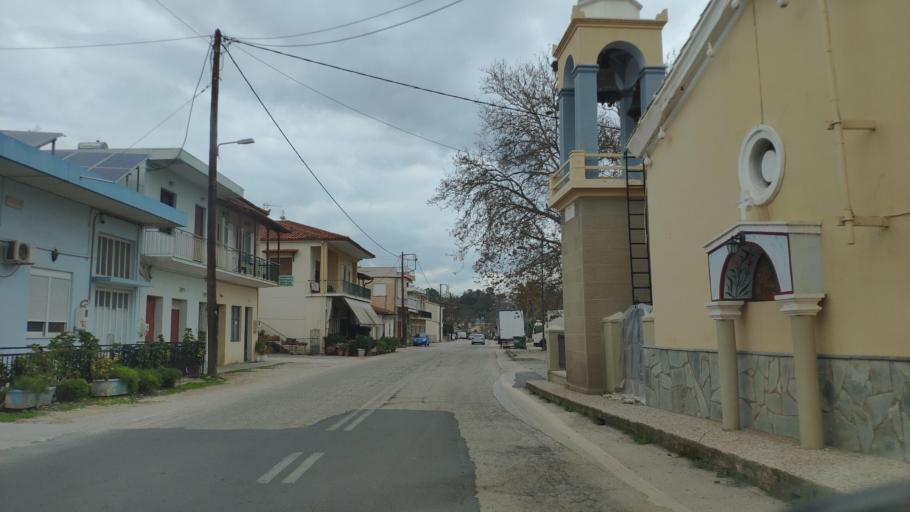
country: GR
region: Peloponnese
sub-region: Nomos Argolidos
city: Nea Kios
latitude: 37.5514
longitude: 22.7168
